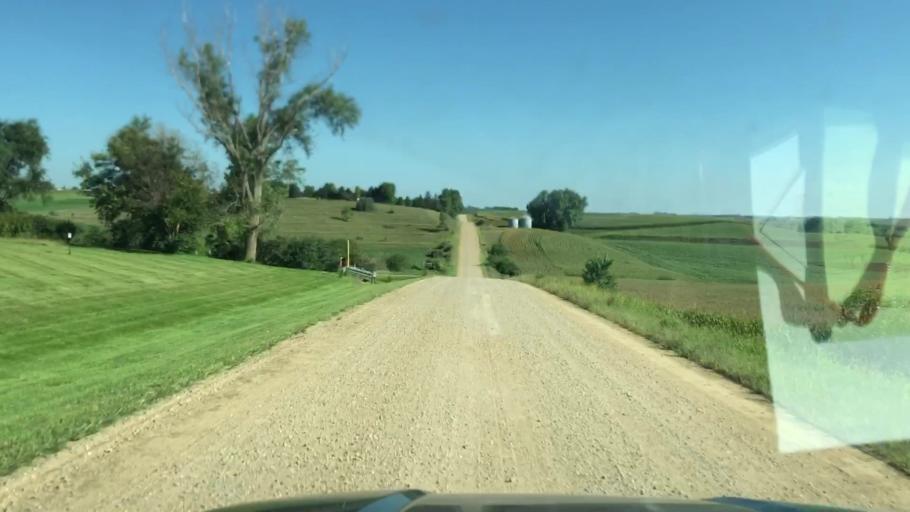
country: US
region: Iowa
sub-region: Woodbury County
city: Sergeant Bluff
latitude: 42.4652
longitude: -96.2922
